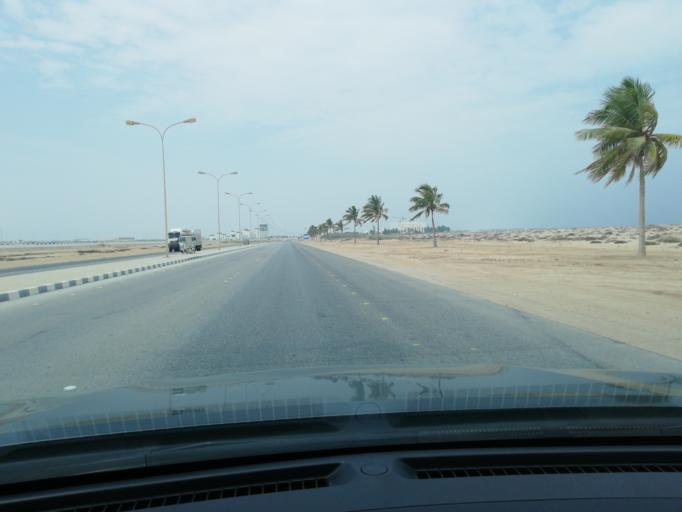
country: OM
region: Zufar
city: Salalah
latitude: 16.9755
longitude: 54.0063
